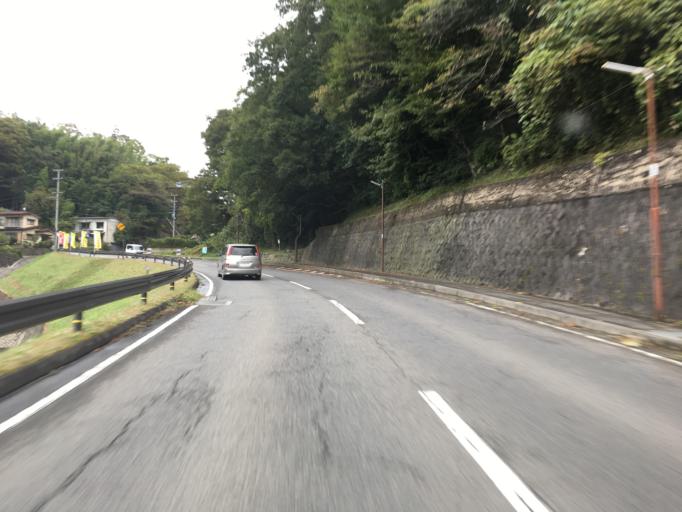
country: JP
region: Fukushima
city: Nihommatsu
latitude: 37.5938
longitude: 140.4289
